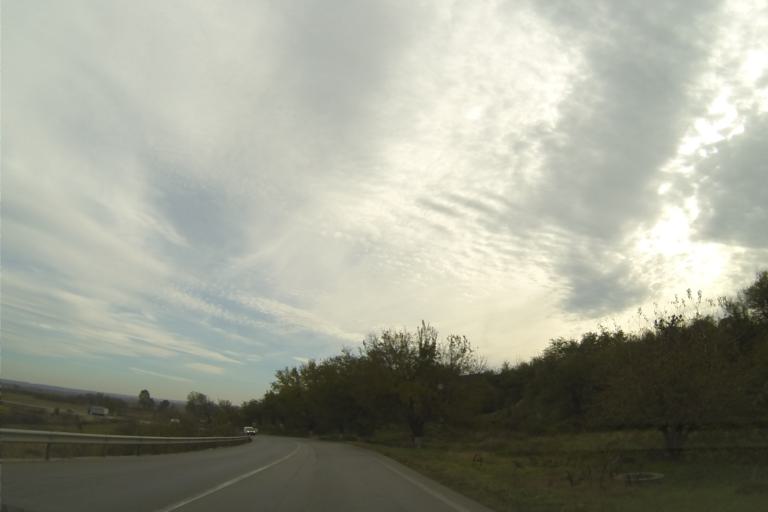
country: RO
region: Olt
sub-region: Comuna Ganeasa
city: Ganeasa
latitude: 44.4016
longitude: 24.2853
